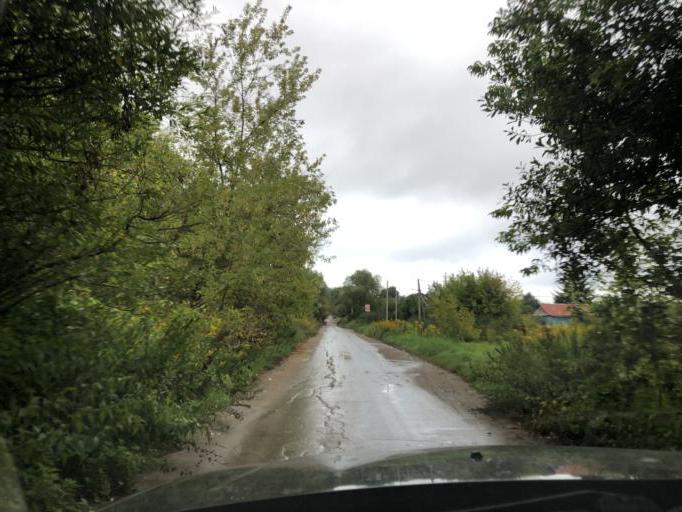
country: RU
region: Tula
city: Mendeleyevskiy
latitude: 54.1727
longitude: 37.5527
